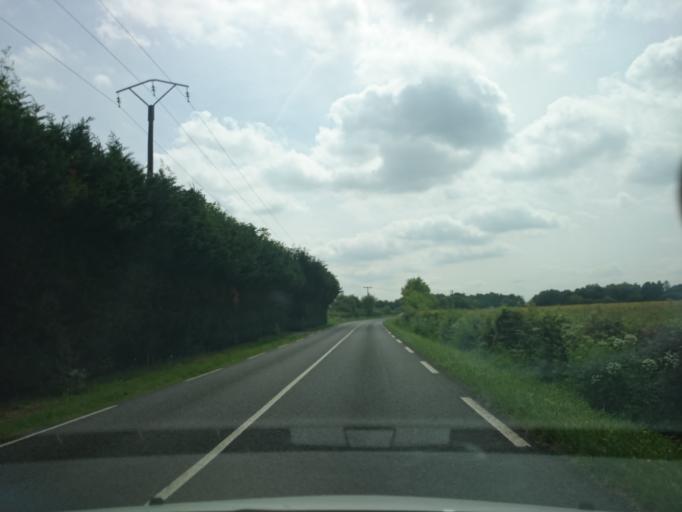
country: FR
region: Pays de la Loire
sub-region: Departement de la Loire-Atlantique
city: Pont-Saint-Martin
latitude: 47.1138
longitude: -1.5809
